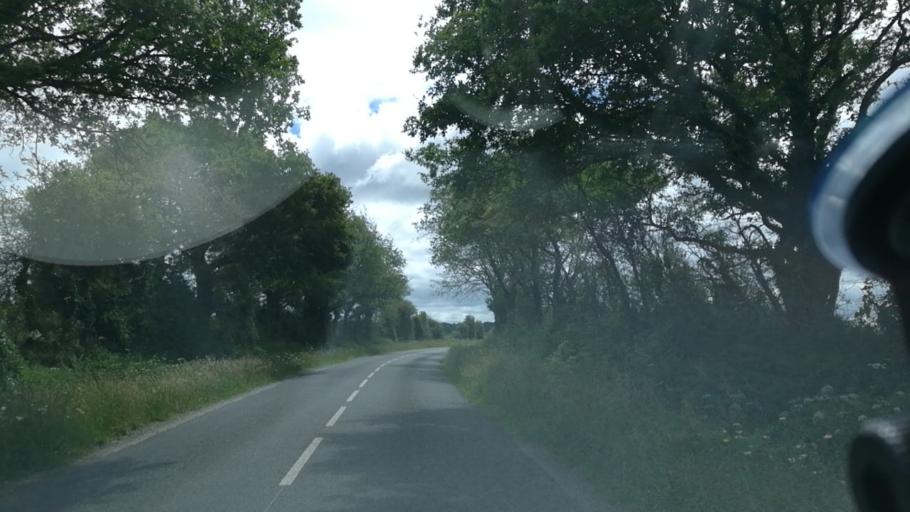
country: FR
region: Pays de la Loire
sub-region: Departement de la Loire-Atlantique
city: Asserac
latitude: 47.4534
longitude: -2.4169
